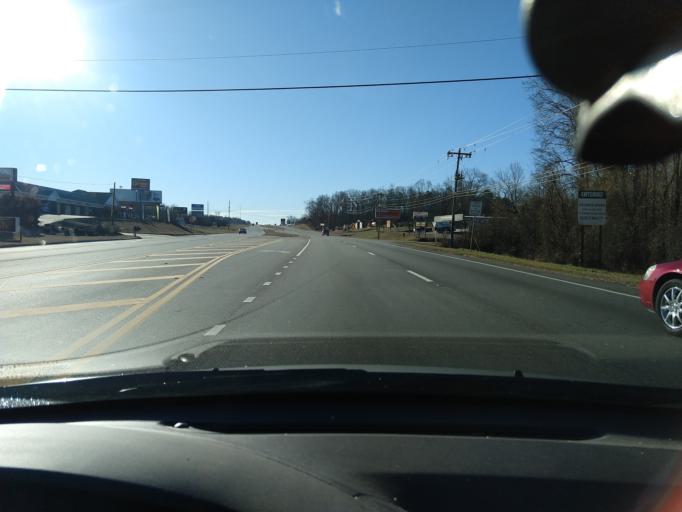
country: US
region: Georgia
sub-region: Jackson County
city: Commerce
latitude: 34.2431
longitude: -83.4578
